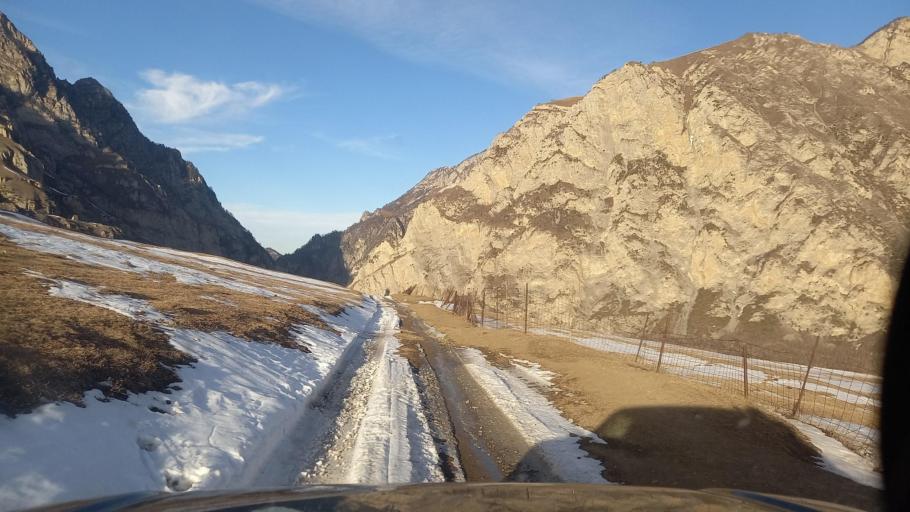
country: RU
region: Ingushetiya
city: Dzhayrakh
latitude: 42.8536
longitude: 44.5154
